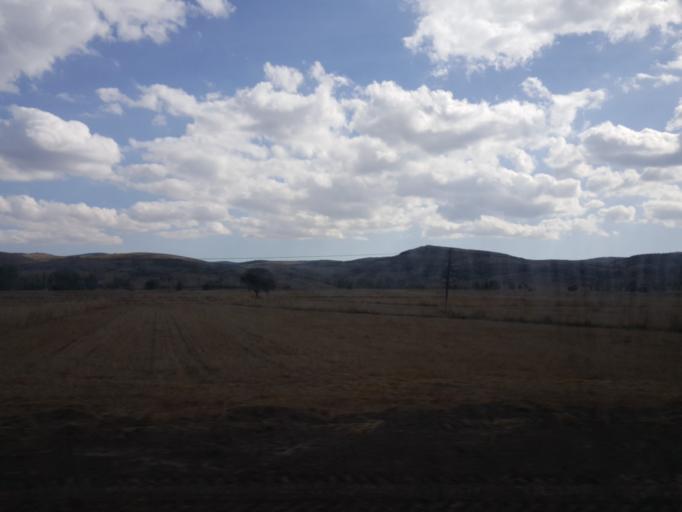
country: TR
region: Tokat
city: Yesilyurt
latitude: 40.0249
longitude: 36.2863
